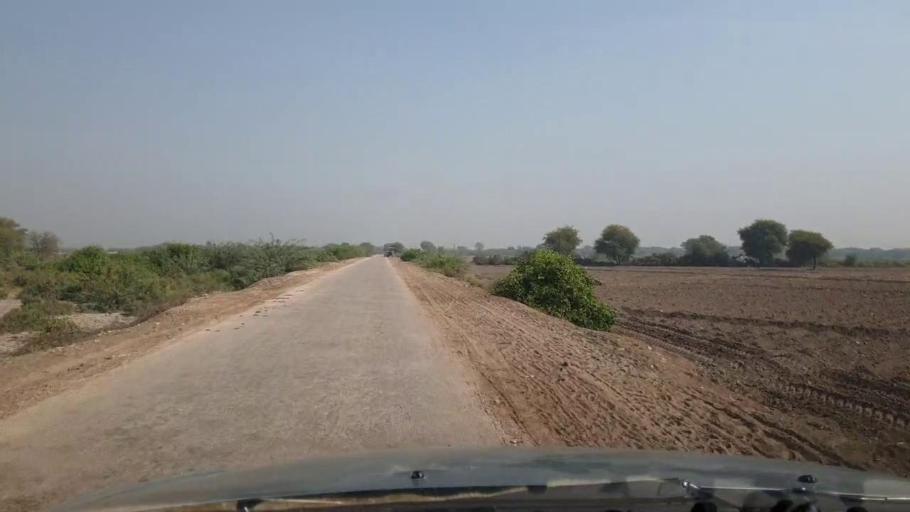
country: PK
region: Sindh
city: Tando Jam
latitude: 25.3026
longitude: 68.5347
